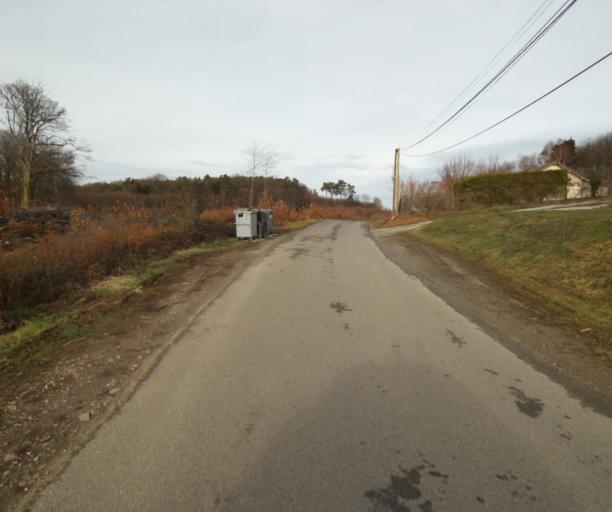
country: FR
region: Limousin
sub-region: Departement de la Correze
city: Saint-Mexant
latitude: 45.2745
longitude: 1.6812
